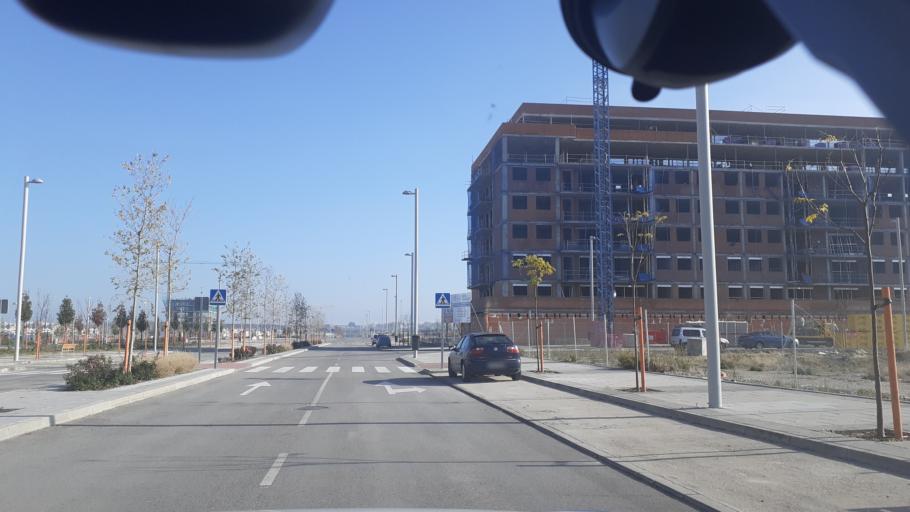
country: ES
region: Madrid
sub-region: Provincia de Madrid
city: Coslada
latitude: 40.3983
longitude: -3.5581
